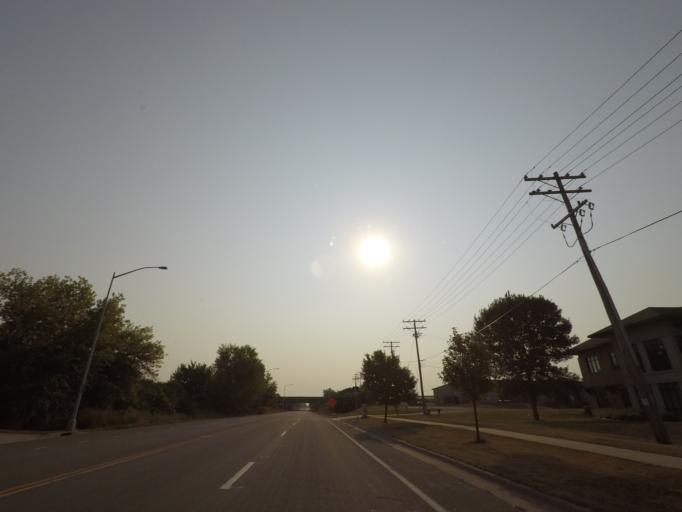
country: US
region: Wisconsin
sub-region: Dane County
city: McFarland
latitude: 43.0518
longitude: -89.2804
